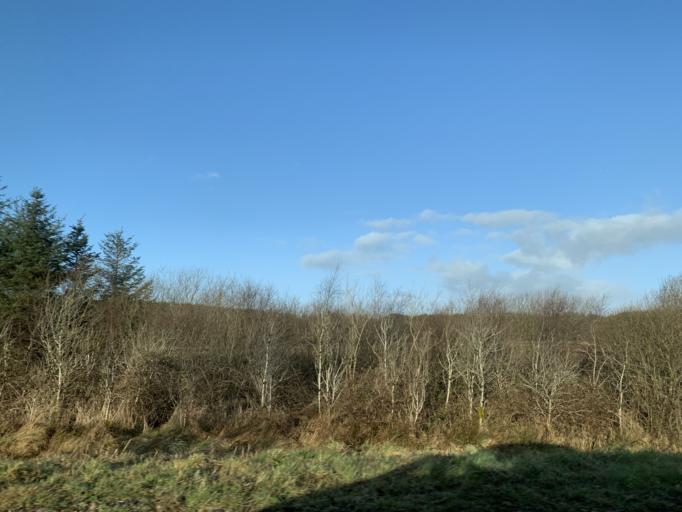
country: IE
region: Connaught
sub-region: Roscommon
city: Ballaghaderreen
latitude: 53.9514
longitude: -8.5447
